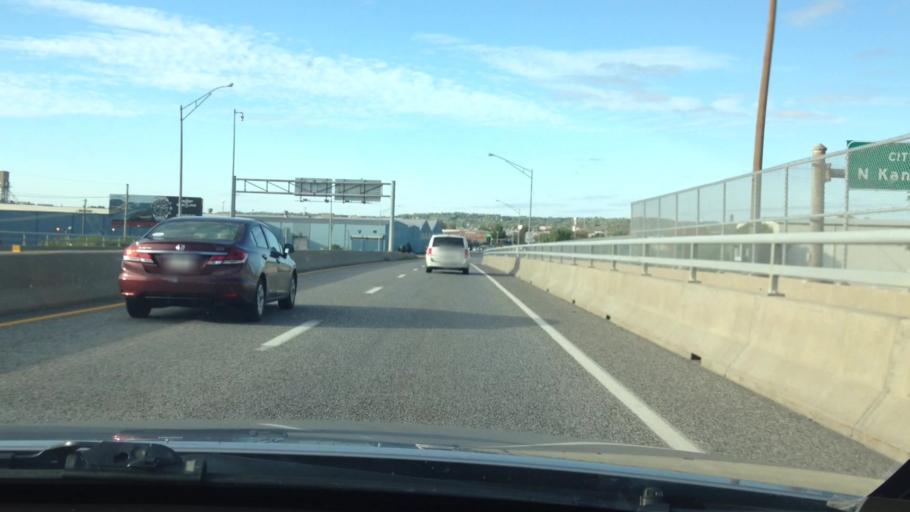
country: US
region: Missouri
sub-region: Clay County
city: North Kansas City
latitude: 39.1232
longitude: -94.5801
